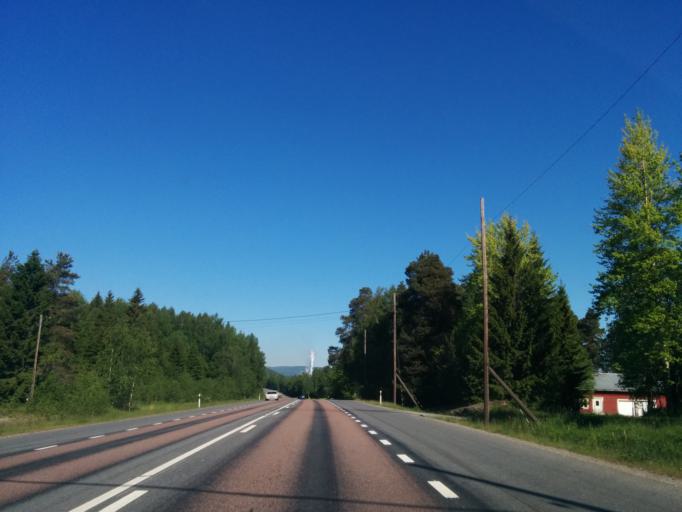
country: SE
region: Vaesternorrland
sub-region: Kramfors Kommun
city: Kramfors
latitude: 62.9542
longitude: 17.7654
